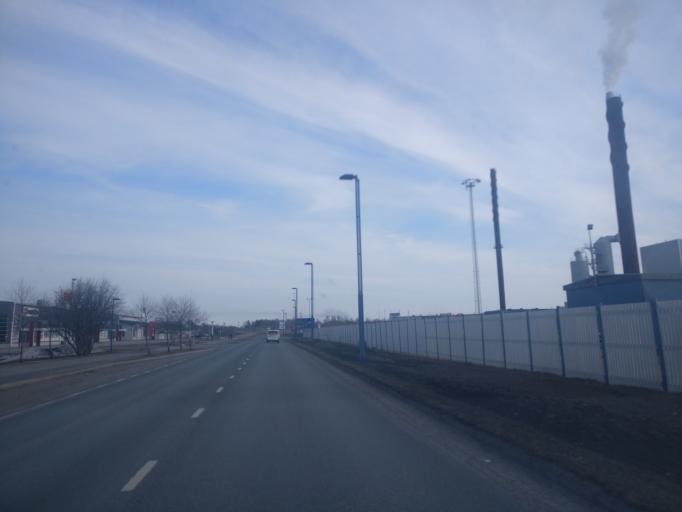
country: FI
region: Lapland
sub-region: Kemi-Tornio
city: Kemi
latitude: 65.7351
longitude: 24.5831
